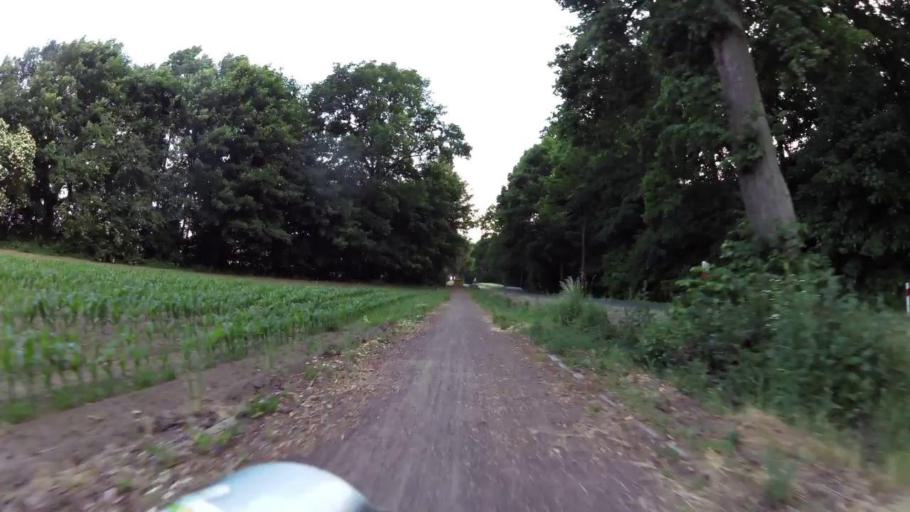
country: PL
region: Kujawsko-Pomorskie
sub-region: Powiat bydgoski
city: Dabrowa Chelminska
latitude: 53.1819
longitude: 18.3325
